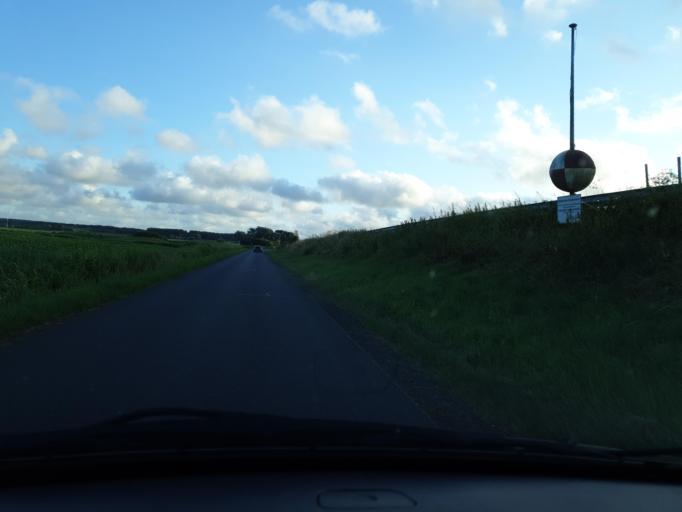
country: DE
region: Schleswig-Holstein
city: Elpersbuttel
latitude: 54.0773
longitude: 9.0250
